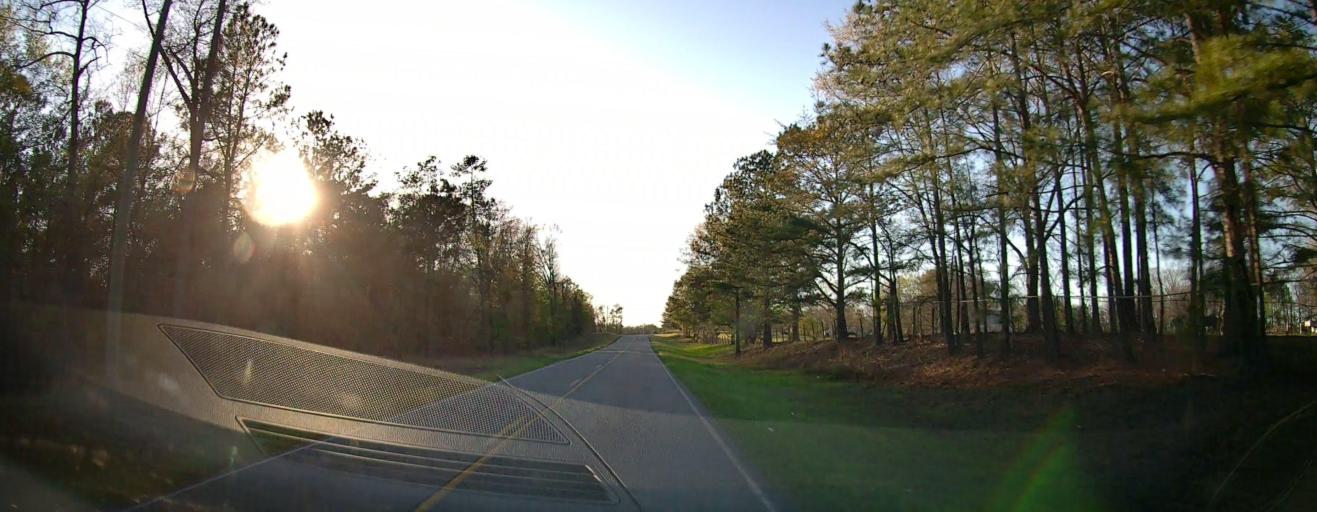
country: US
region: Georgia
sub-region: Wilkinson County
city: Gordon
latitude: 32.8794
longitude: -83.2747
